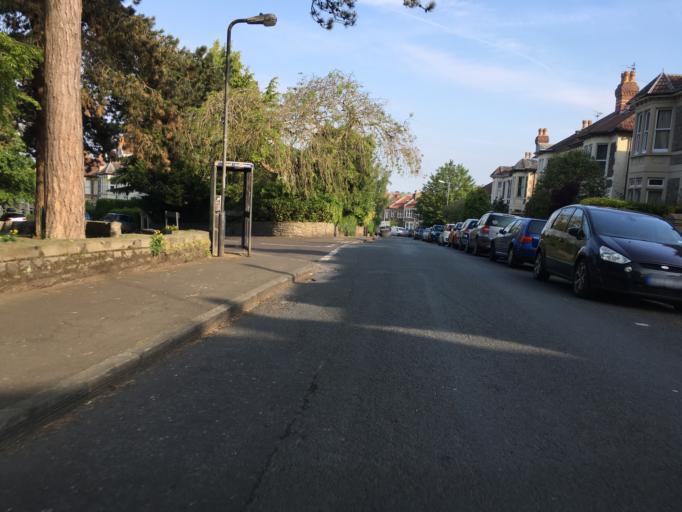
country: GB
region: England
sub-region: Bristol
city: Bristol
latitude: 51.4740
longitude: -2.5861
